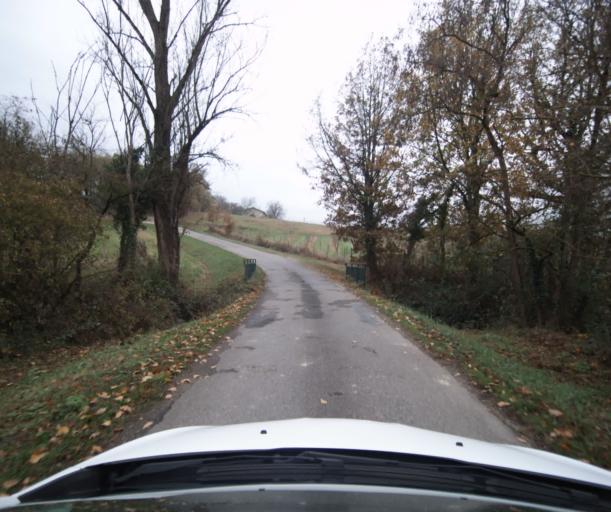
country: FR
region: Midi-Pyrenees
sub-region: Departement du Tarn-et-Garonne
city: Moissac
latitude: 44.0791
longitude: 1.1588
